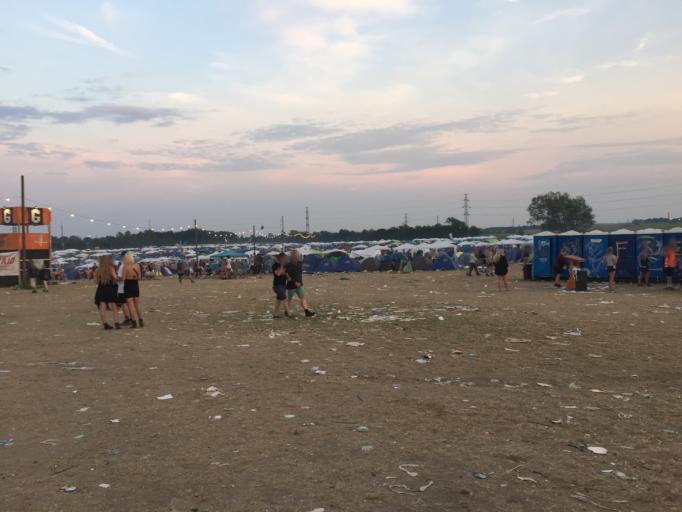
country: DK
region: Zealand
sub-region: Roskilde Kommune
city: Roskilde
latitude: 55.6172
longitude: 12.0753
